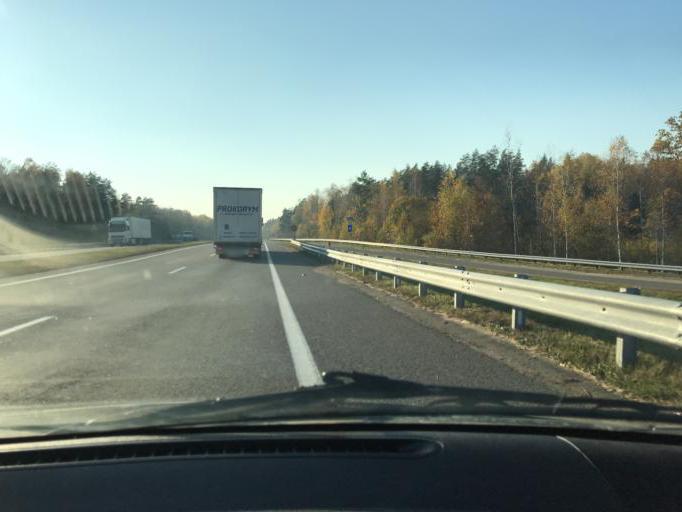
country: BY
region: Minsk
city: Loshnitsa
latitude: 54.2991
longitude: 28.9287
